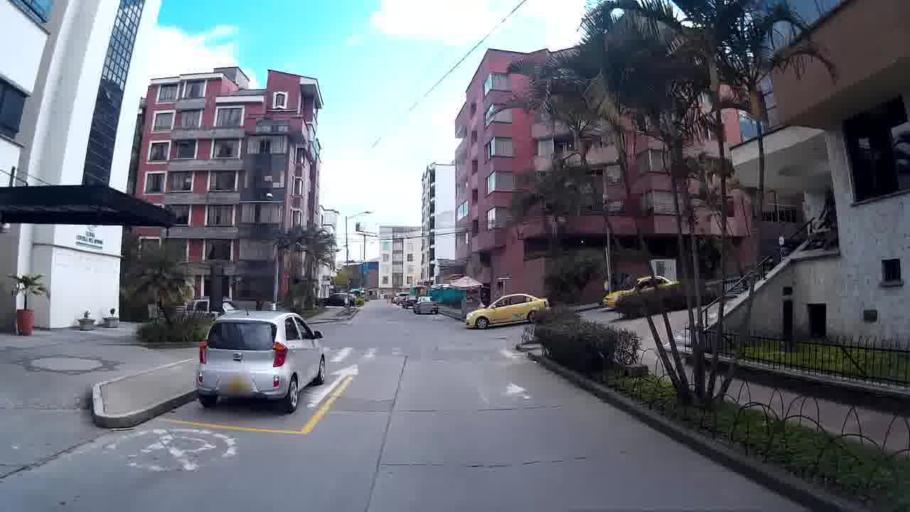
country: CO
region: Quindio
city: Armenia
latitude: 4.5450
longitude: -75.6614
